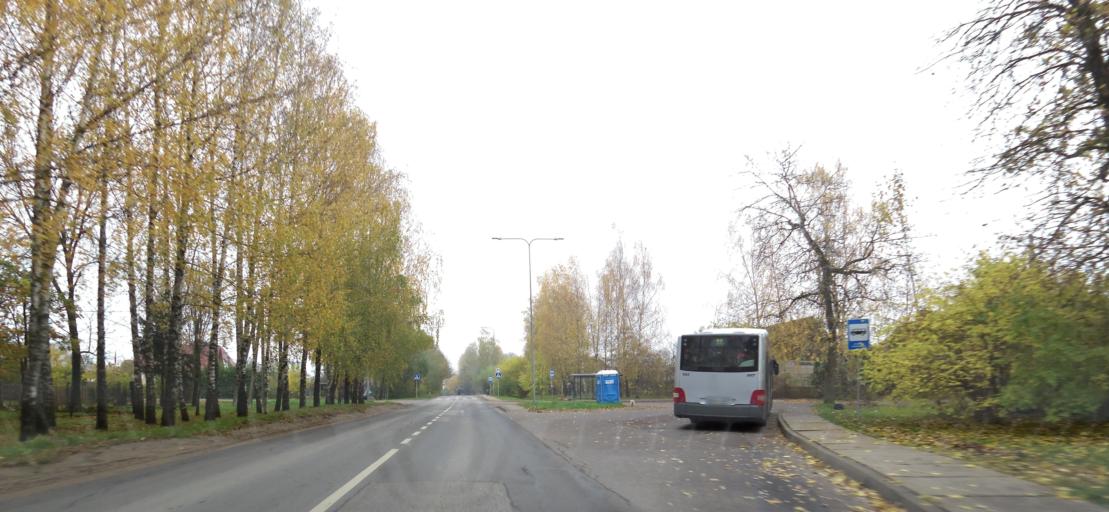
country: LT
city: Skaidiskes
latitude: 54.6592
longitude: 25.3638
